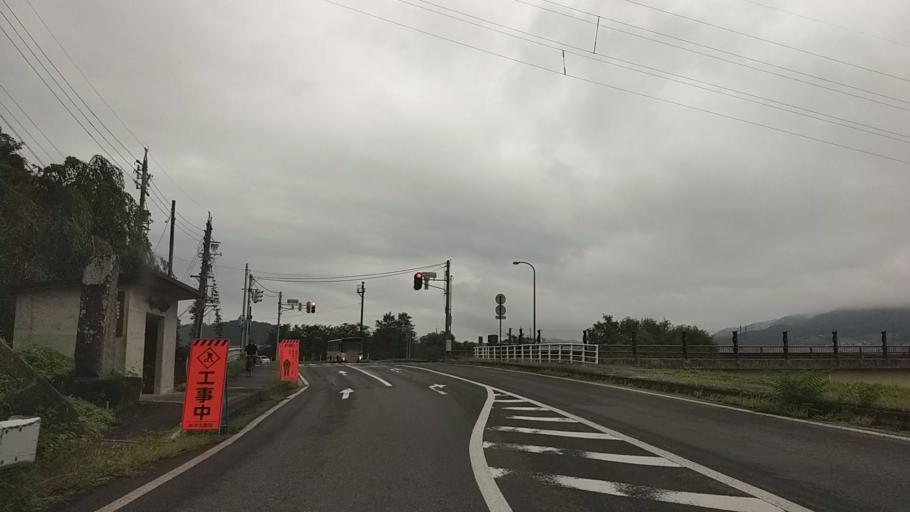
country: JP
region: Nagano
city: Iiyama
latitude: 36.8416
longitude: 138.3665
